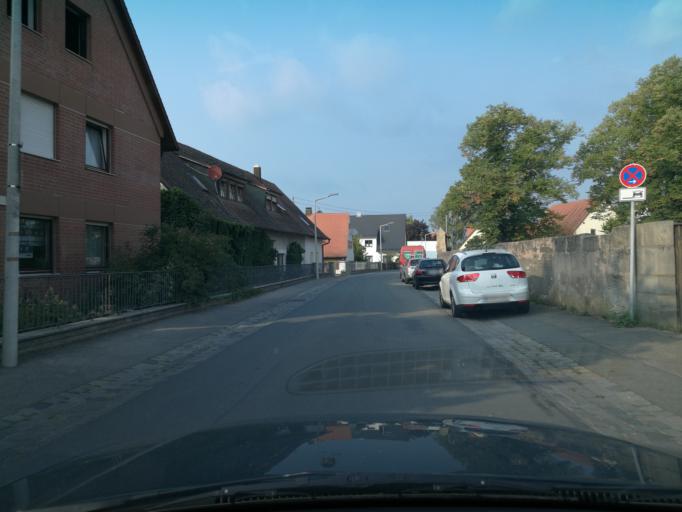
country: DE
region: Bavaria
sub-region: Regierungsbezirk Mittelfranken
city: Wetzendorf
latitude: 49.4915
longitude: 11.0618
